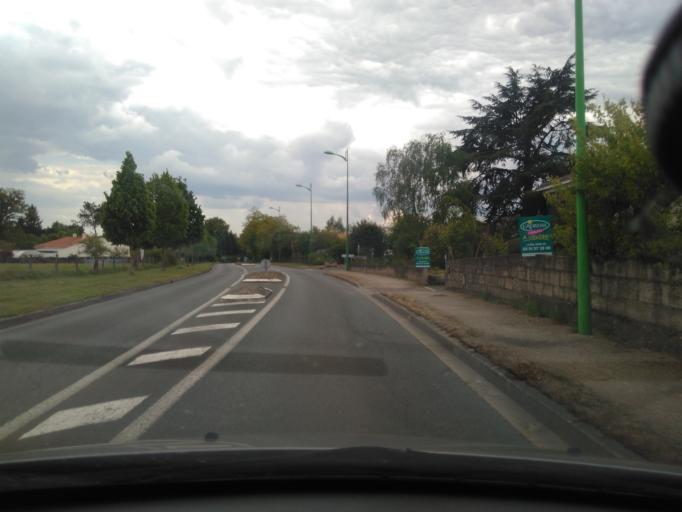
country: FR
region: Pays de la Loire
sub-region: Departement de la Vendee
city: Dompierre-sur-Yon
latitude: 46.7325
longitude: -1.3921
